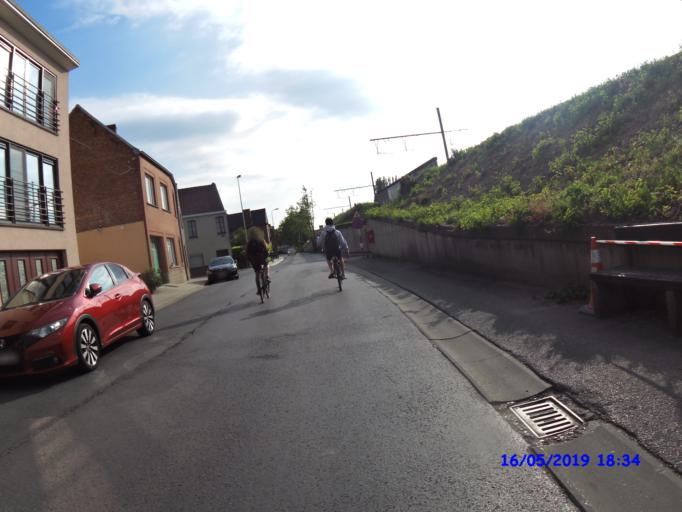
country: BE
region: Flanders
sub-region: Provincie West-Vlaanderen
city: Waregem
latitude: 50.8897
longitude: 3.4210
